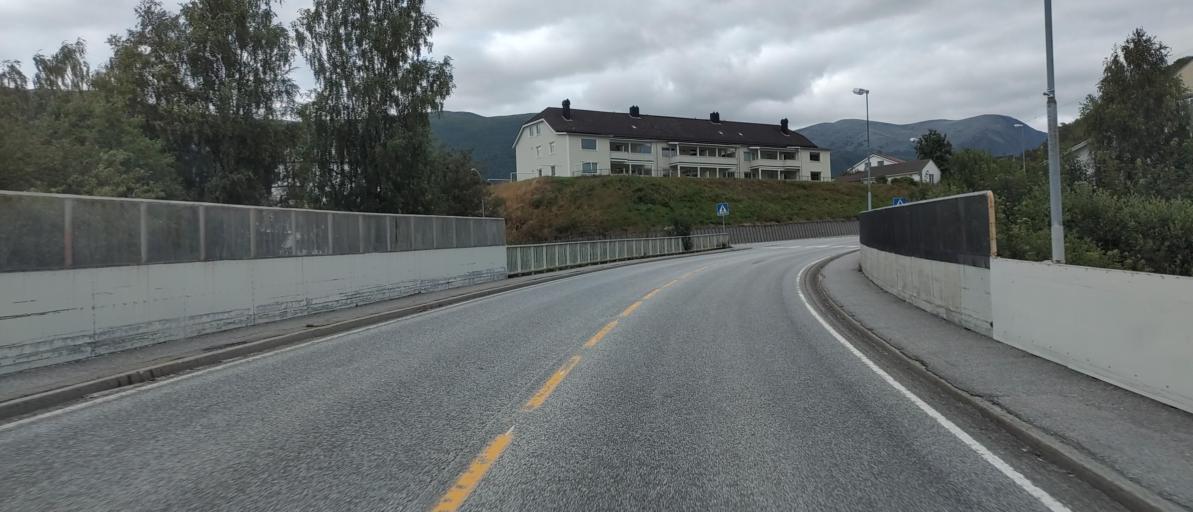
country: NO
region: More og Romsdal
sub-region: Rauma
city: Andalsnes
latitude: 62.5611
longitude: 7.6849
